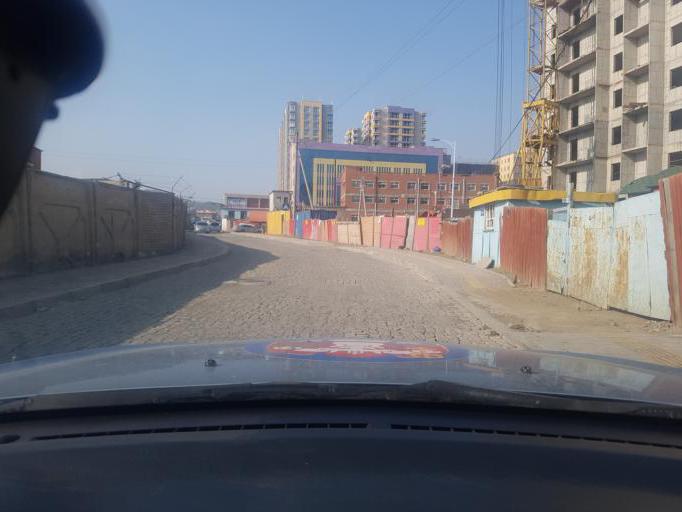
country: MN
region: Ulaanbaatar
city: Ulaanbaatar
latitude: 47.9225
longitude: 106.9667
